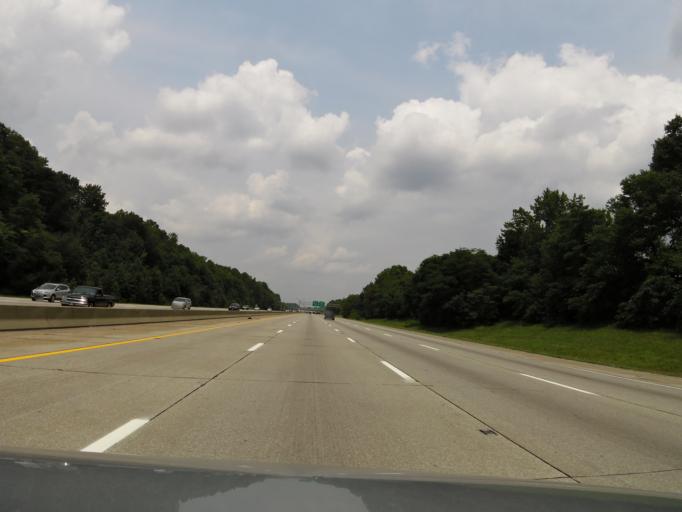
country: US
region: Kentucky
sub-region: Jefferson County
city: Heritage Creek
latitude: 38.1023
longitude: -85.7009
